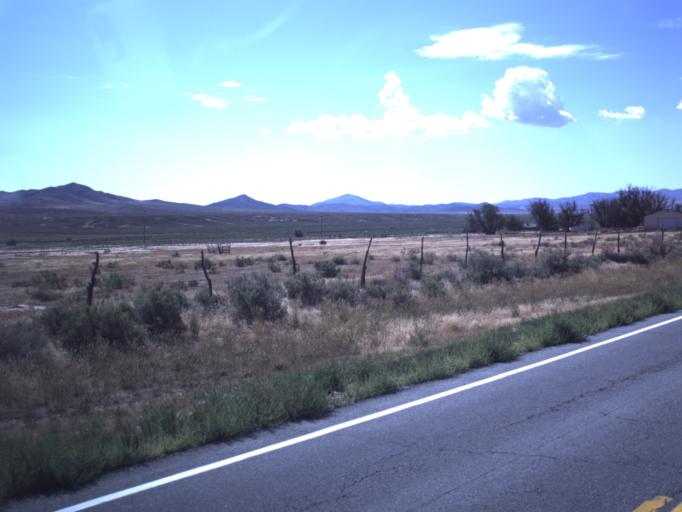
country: US
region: Utah
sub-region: Tooele County
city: Tooele
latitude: 40.1766
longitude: -112.4261
